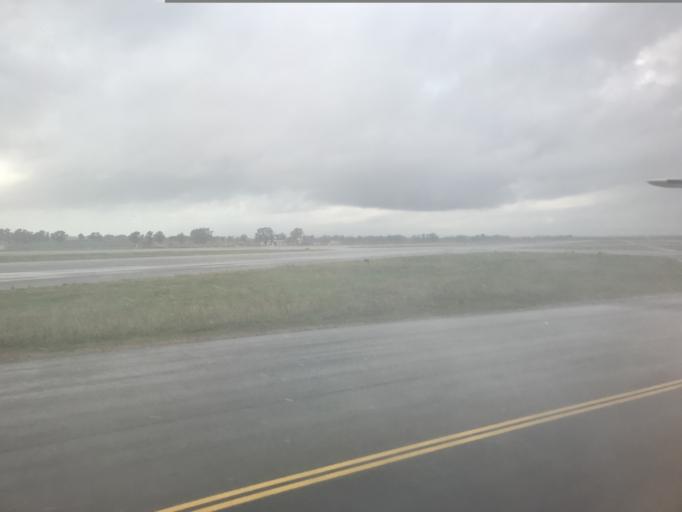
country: IT
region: Latium
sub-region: Citta metropolitana di Roma Capitale
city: Npp 23 (Parco Leonardo)
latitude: 41.8252
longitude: 12.2683
